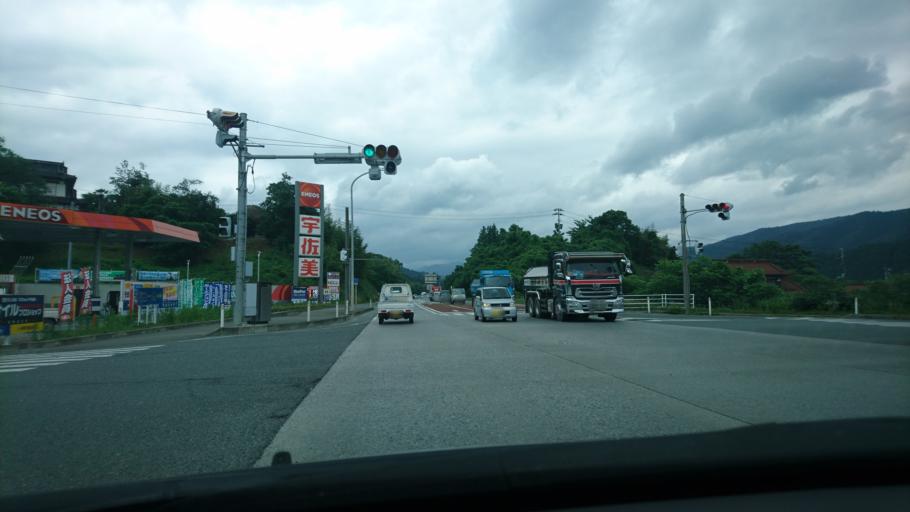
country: JP
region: Iwate
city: Ofunato
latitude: 38.9014
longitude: 141.5499
